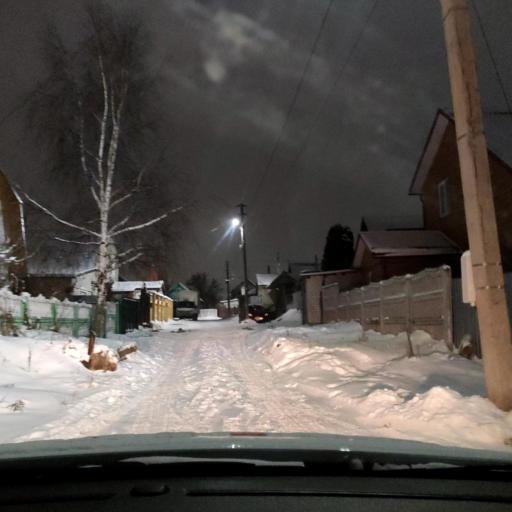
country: RU
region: Tatarstan
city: Staroye Arakchino
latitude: 55.8813
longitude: 49.0437
